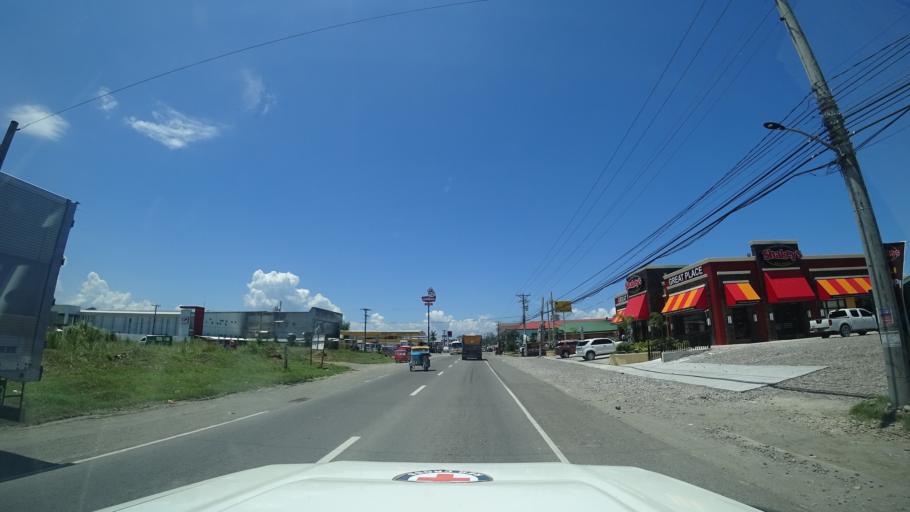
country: PH
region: Eastern Visayas
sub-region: Province of Leyte
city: Pawing
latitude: 11.1768
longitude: 125.0014
